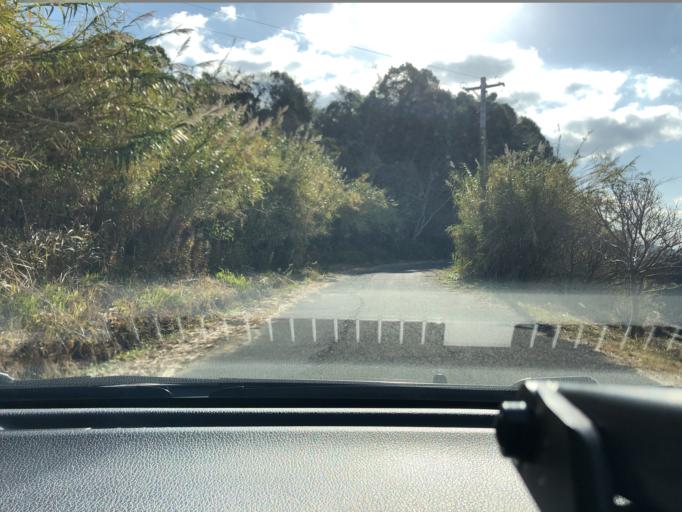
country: JP
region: Kochi
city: Sukumo
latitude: 32.9153
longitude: 132.6879
